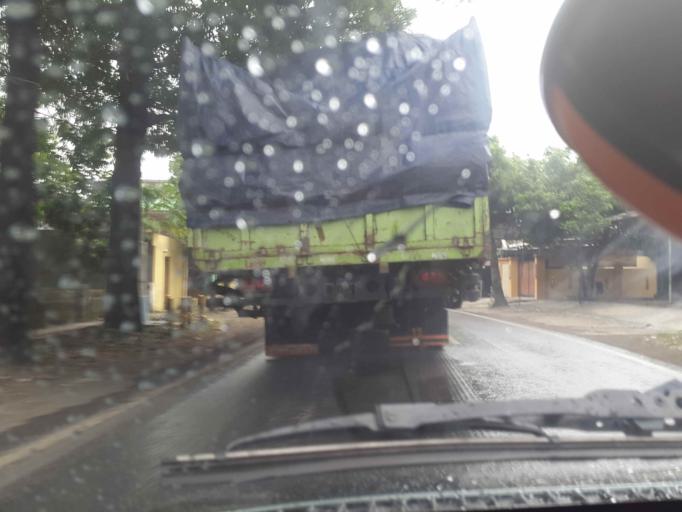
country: ID
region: Central Java
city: Sragen
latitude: -7.4327
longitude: 111.0333
